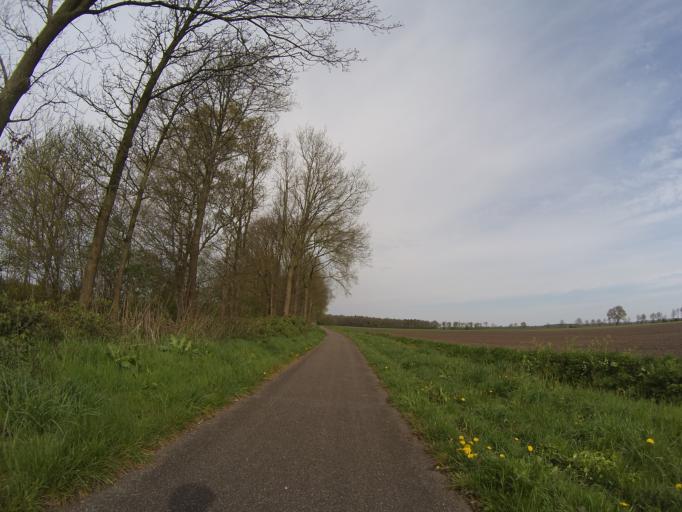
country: NL
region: Drenthe
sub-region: Gemeente Coevorden
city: Sleen
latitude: 52.8320
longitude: 6.6837
